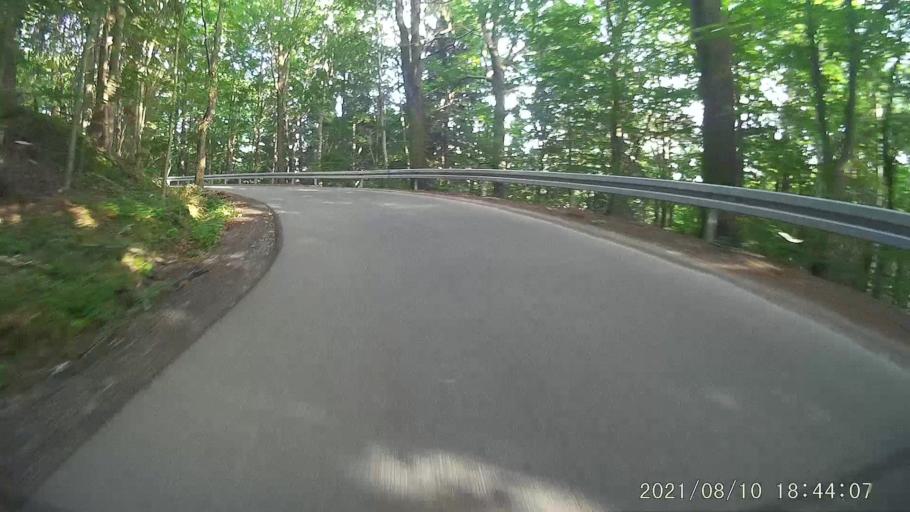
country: PL
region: Lower Silesian Voivodeship
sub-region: Powiat klodzki
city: Duszniki-Zdroj
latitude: 50.4441
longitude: 16.3445
